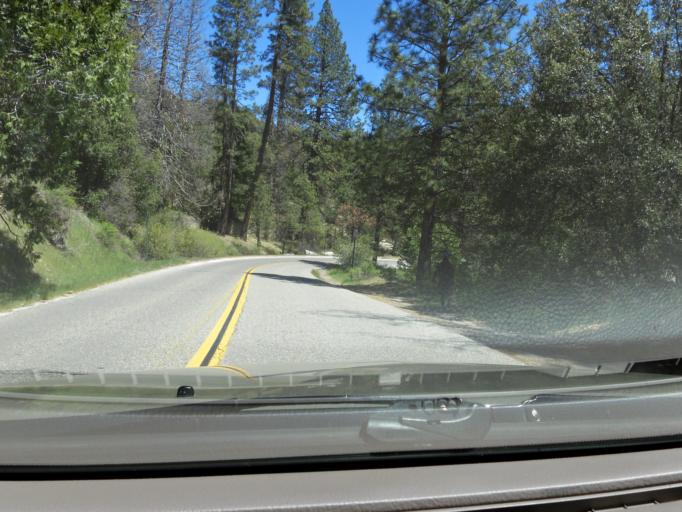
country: US
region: California
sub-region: Madera County
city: Oakhurst
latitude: 37.3319
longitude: -119.5725
